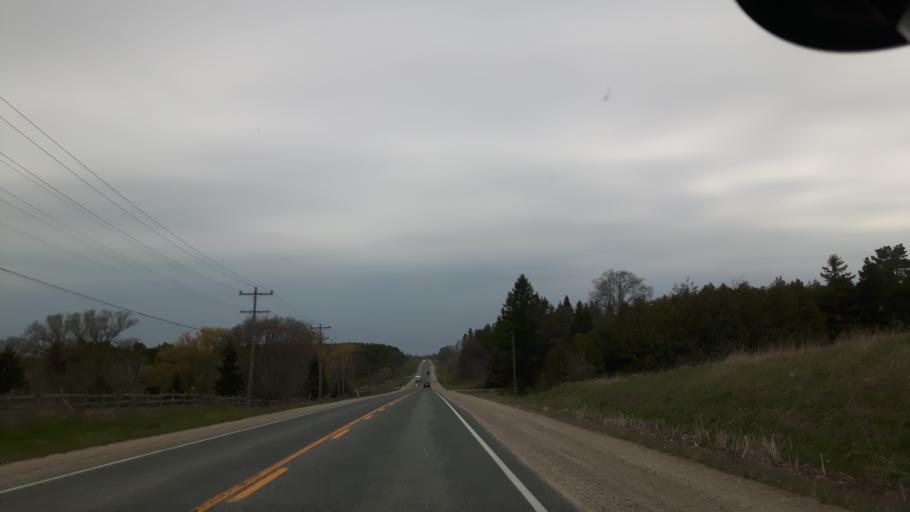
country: CA
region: Ontario
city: Goderich
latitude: 43.6658
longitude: -81.6206
